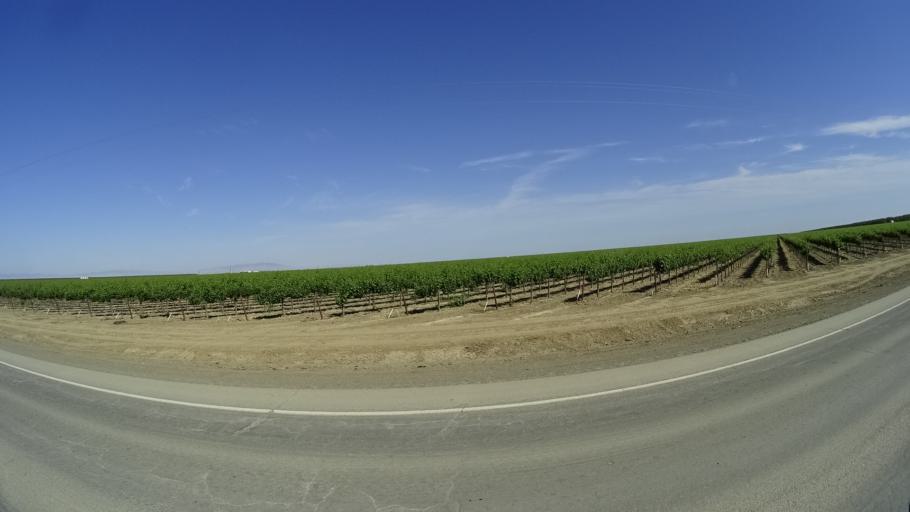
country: US
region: California
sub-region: Kings County
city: Lemoore Station
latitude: 36.1636
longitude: -119.9784
